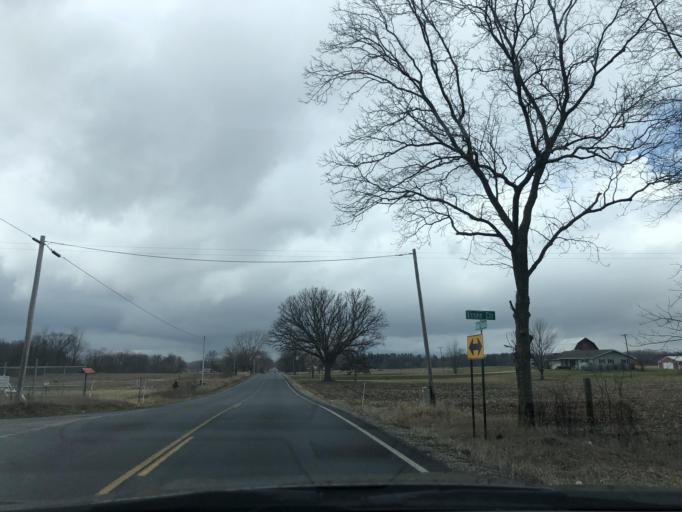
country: US
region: Michigan
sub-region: Clinton County
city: Fowler
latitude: 43.1045
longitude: -84.6598
